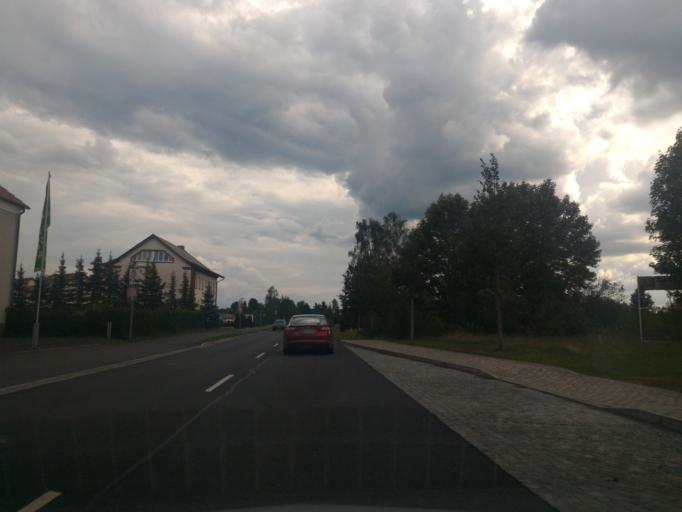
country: DE
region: Saxony
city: Weisskeissel
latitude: 51.4988
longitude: 14.7150
